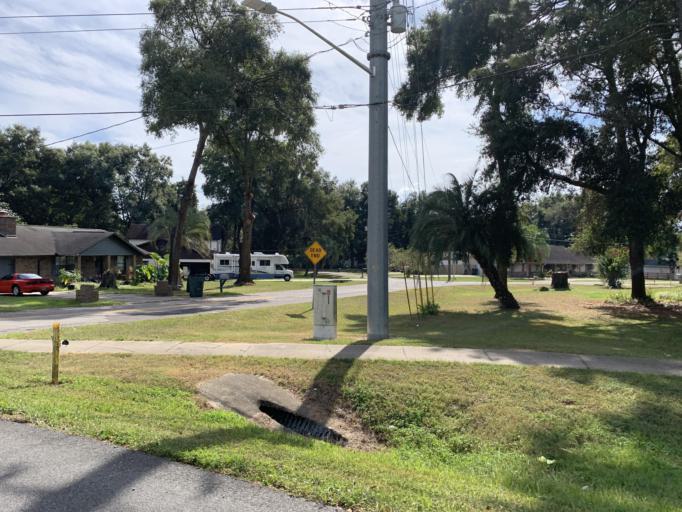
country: US
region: Florida
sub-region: Marion County
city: Silver Springs Shores
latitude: 29.1608
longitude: -82.0664
